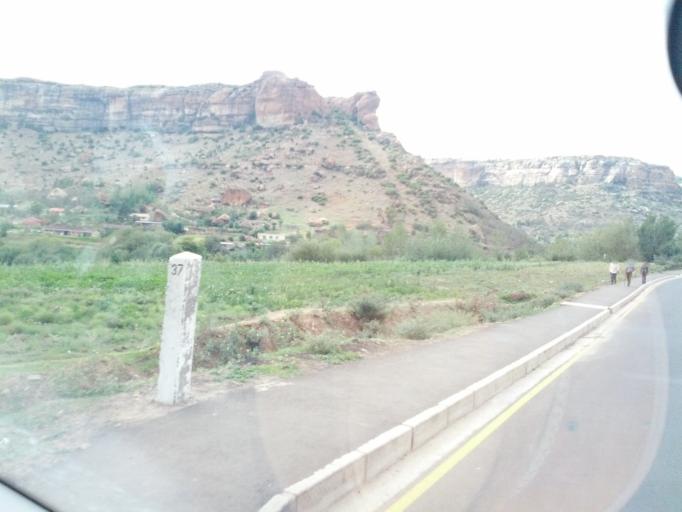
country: LS
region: Maseru
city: Nako
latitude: -29.4706
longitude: 27.7386
